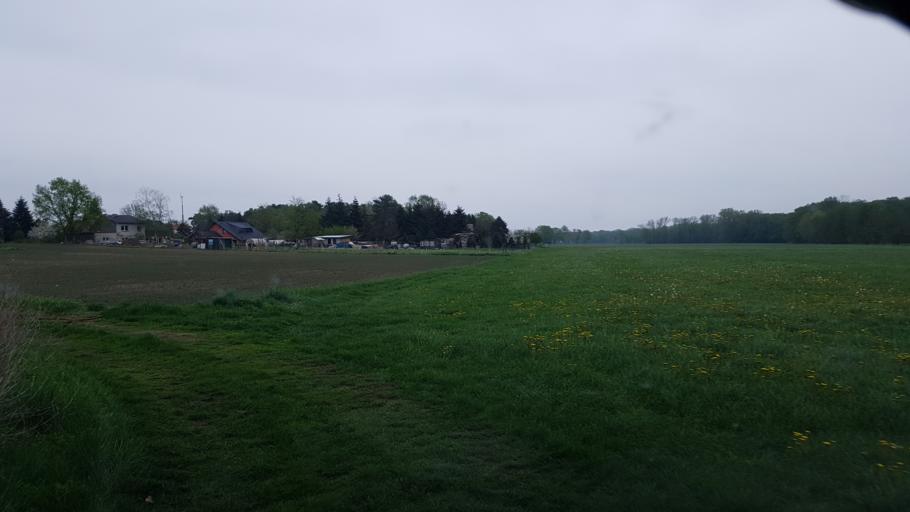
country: DE
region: Brandenburg
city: Schonewalde
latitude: 51.6986
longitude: 13.6077
